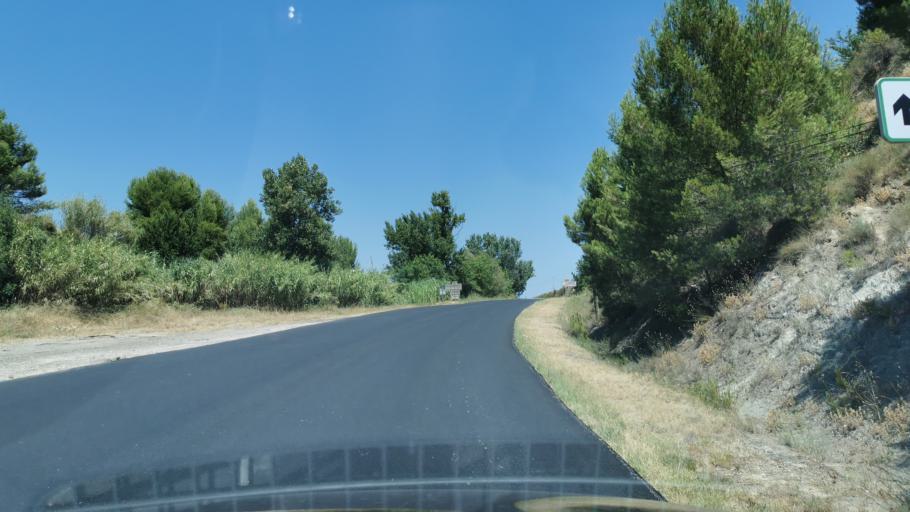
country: FR
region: Languedoc-Roussillon
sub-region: Departement de l'Herault
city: Cazouls-les-Beziers
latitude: 43.3977
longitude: 3.1029
